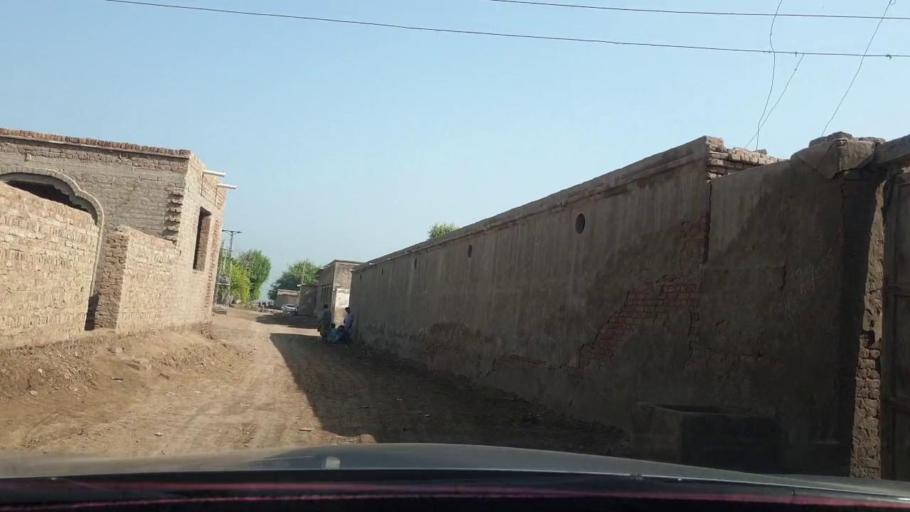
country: PK
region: Sindh
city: Kambar
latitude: 27.6038
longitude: 67.9358
